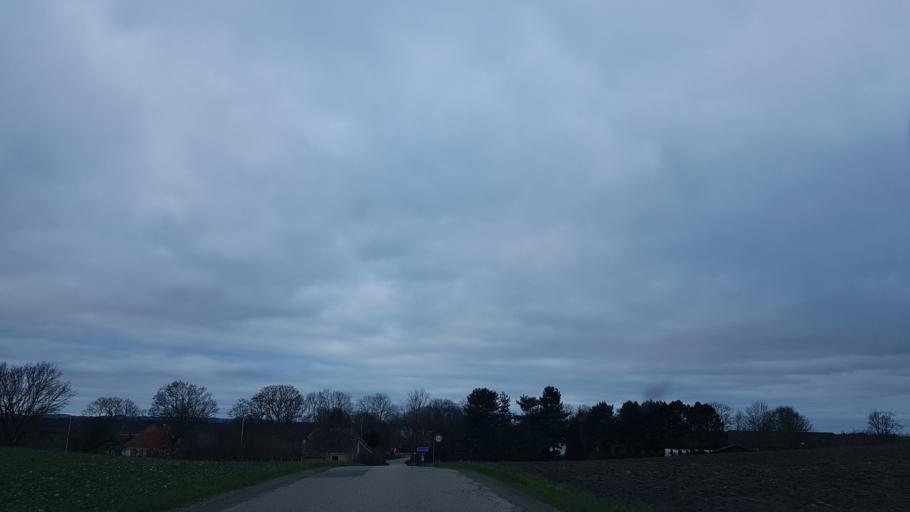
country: DK
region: Zealand
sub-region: Odsherred Kommune
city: Hojby
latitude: 55.9288
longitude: 11.5580
